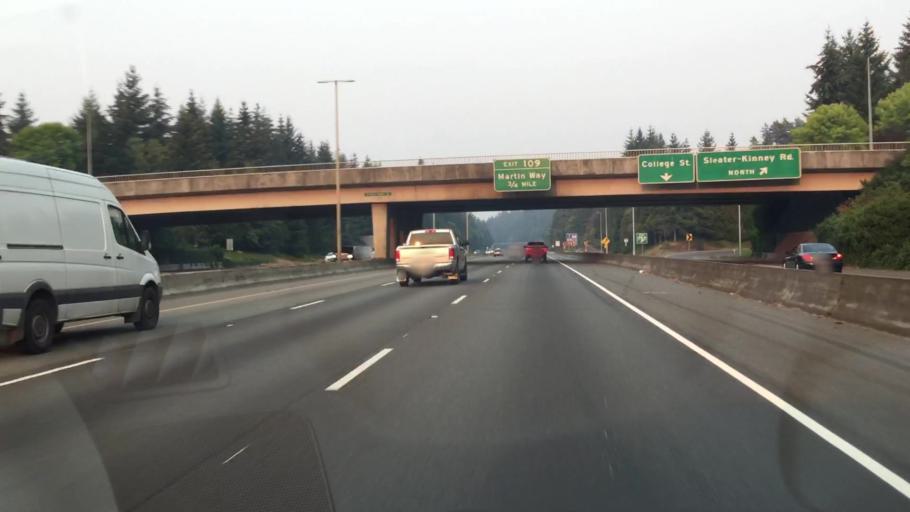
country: US
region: Washington
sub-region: Thurston County
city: Lacey
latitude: 47.0457
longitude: -122.8347
